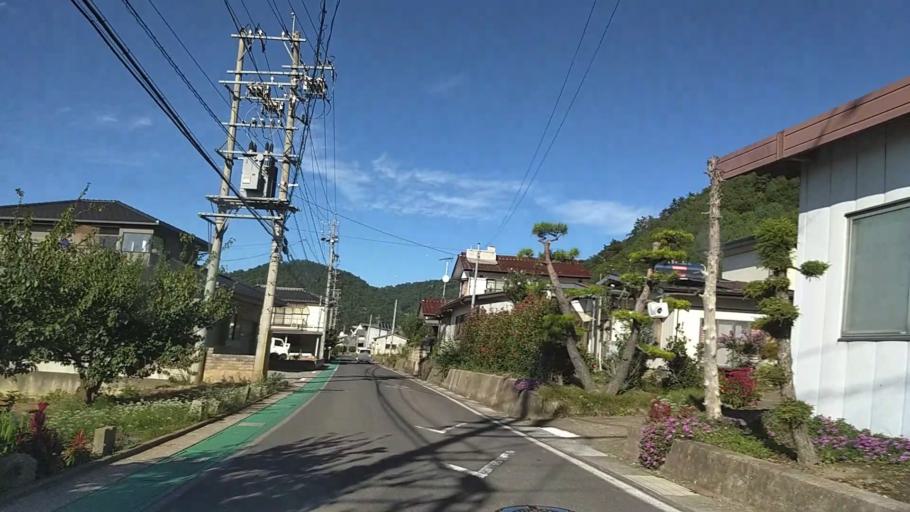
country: JP
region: Nagano
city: Nagano-shi
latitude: 36.5482
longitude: 138.1539
